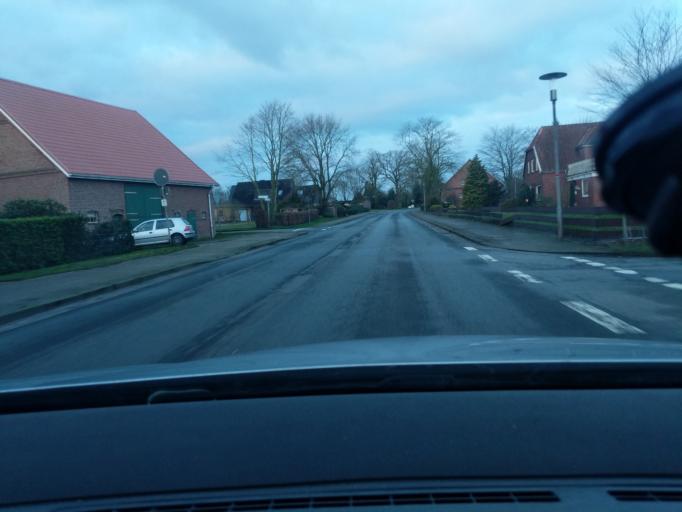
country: DE
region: Lower Saxony
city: Lintig
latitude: 53.6048
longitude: 8.8927
